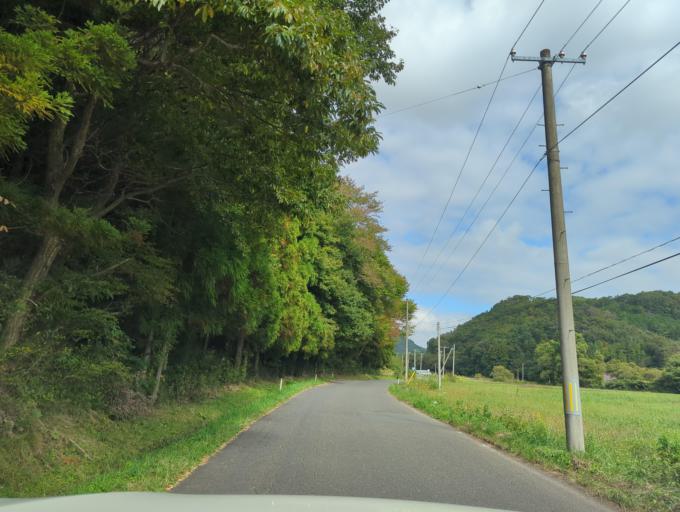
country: JP
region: Fukushima
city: Motomiya
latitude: 37.4992
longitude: 140.3256
